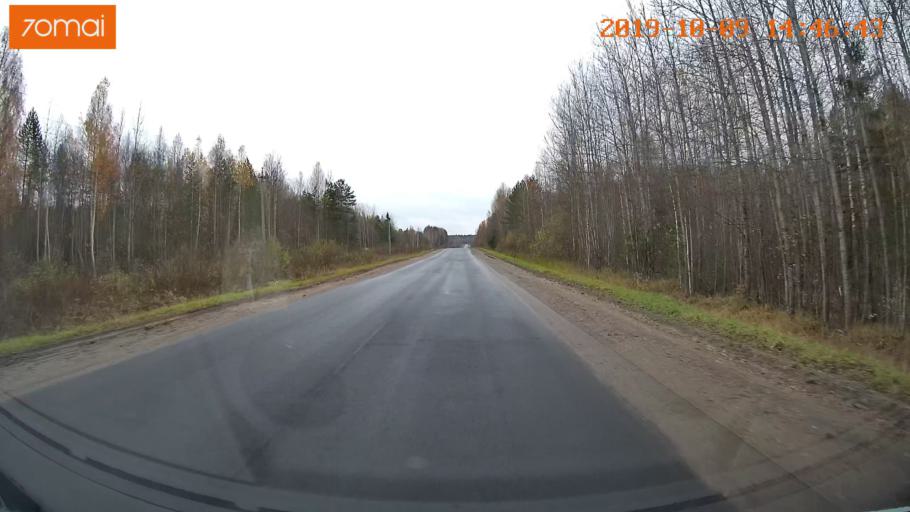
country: RU
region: Kostroma
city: Buy
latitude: 58.4274
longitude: 41.5757
